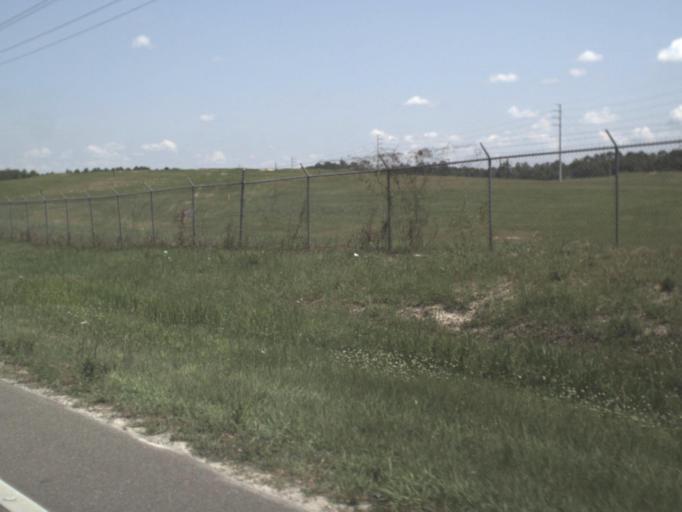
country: US
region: Florida
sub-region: Clay County
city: Keystone Heights
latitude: 29.8065
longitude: -82.0641
